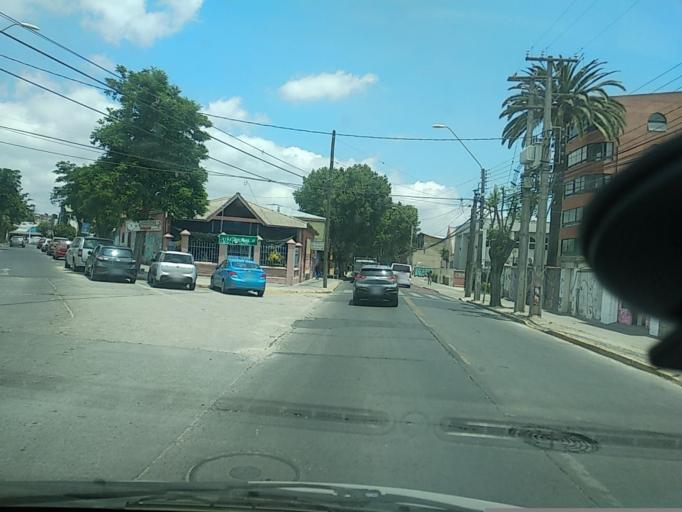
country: CL
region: Valparaiso
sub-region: Provincia de Marga Marga
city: Quilpue
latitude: -33.0450
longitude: -71.4379
